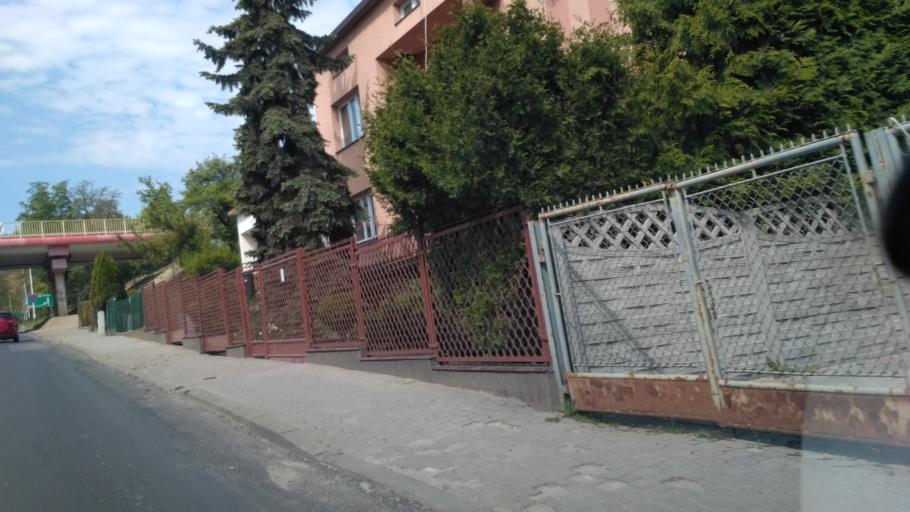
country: PL
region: Subcarpathian Voivodeship
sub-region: Powiat jaroslawski
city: Jaroslaw
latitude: 50.0177
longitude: 22.6877
